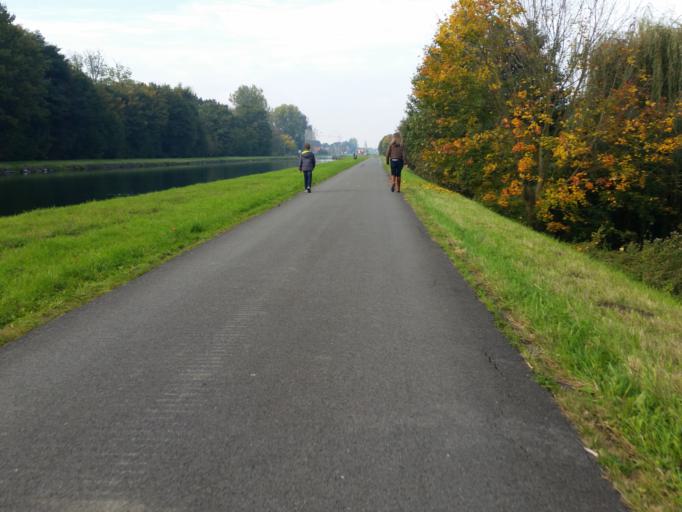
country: BE
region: Flanders
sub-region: Provincie Antwerpen
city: Bonheiden
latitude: 50.9987
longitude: 4.5151
